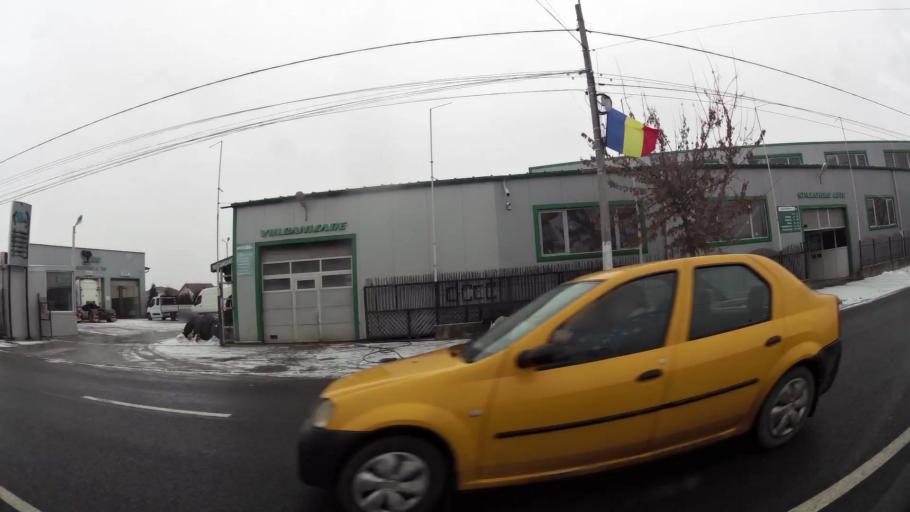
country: RO
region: Dambovita
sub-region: Municipiul Targoviste
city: Targoviste
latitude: 44.9379
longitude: 25.4427
